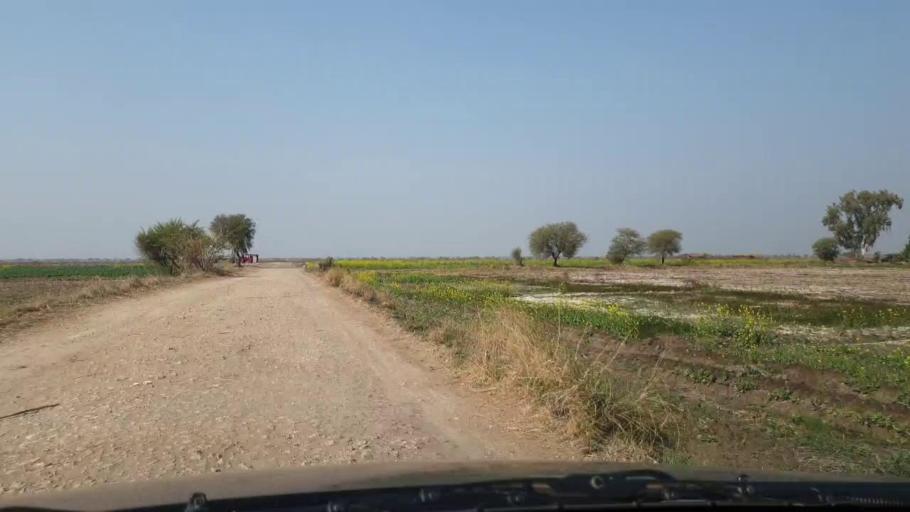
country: PK
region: Sindh
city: Jhol
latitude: 25.8615
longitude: 68.9965
